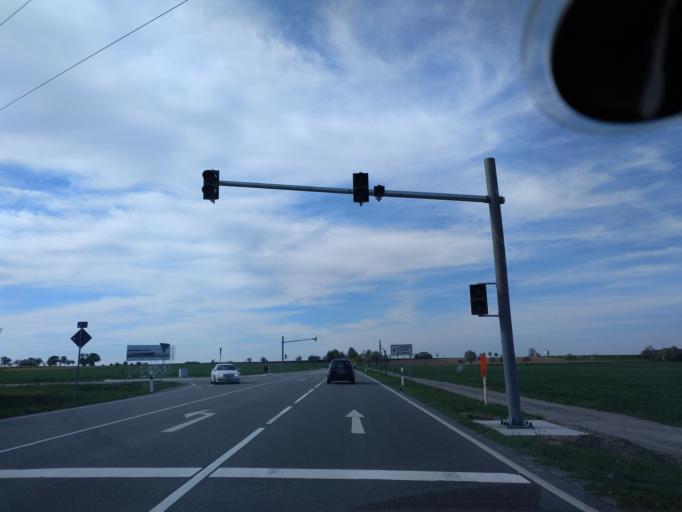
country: DE
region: Baden-Wuerttemberg
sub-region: Regierungsbezirk Stuttgart
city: Kupferzell
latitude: 49.2057
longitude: 9.6834
